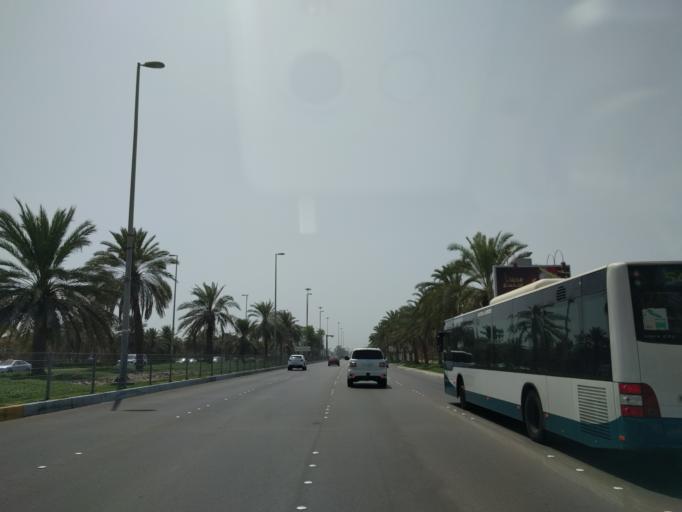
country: AE
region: Abu Dhabi
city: Abu Dhabi
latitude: 24.4363
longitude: 54.4203
